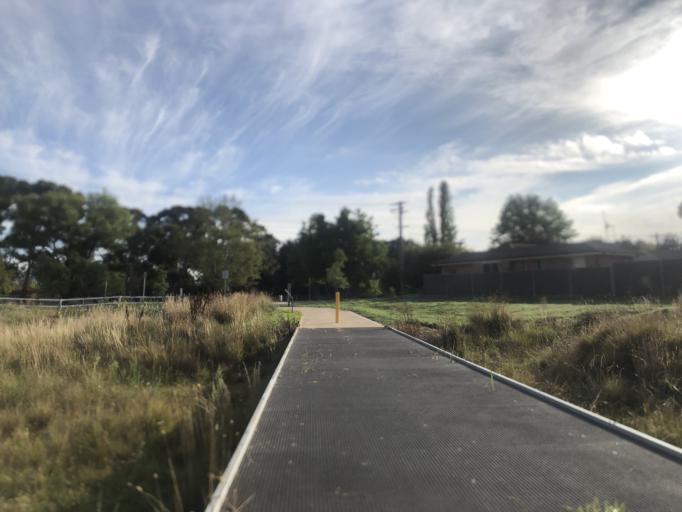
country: AU
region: New South Wales
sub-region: Orange Municipality
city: Orange
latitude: -33.2941
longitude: 149.0930
